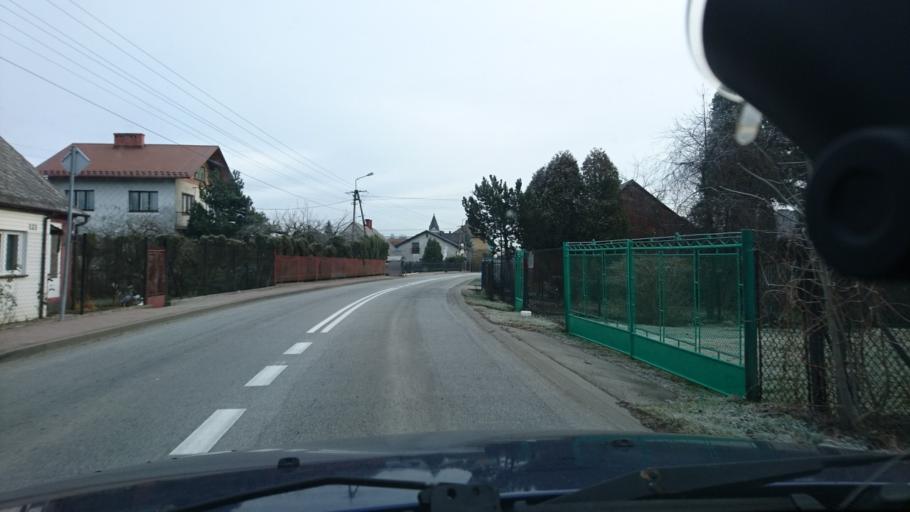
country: PL
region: Silesian Voivodeship
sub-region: Powiat bielski
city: Rybarzowice
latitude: 49.7301
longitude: 19.0977
